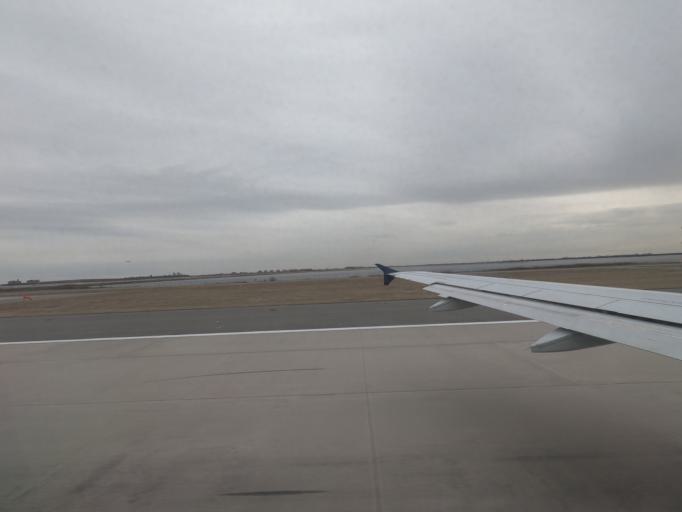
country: US
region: New York
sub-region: Nassau County
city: Inwood
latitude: 40.6337
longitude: -73.7843
